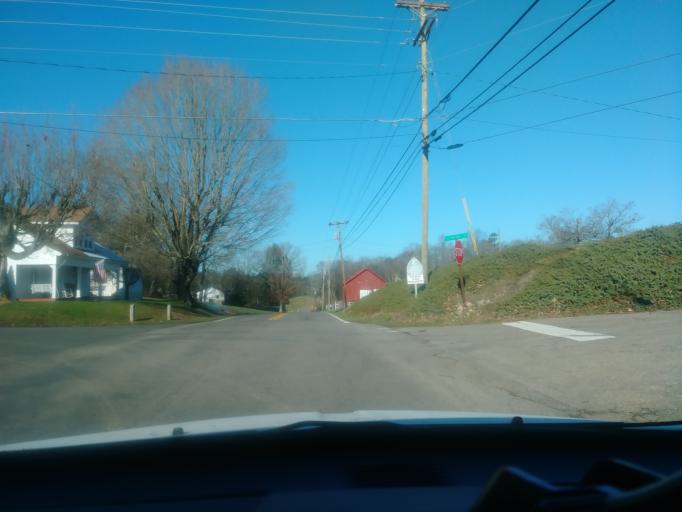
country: US
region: Tennessee
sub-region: Greene County
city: Mosheim
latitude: 36.1170
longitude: -82.9663
